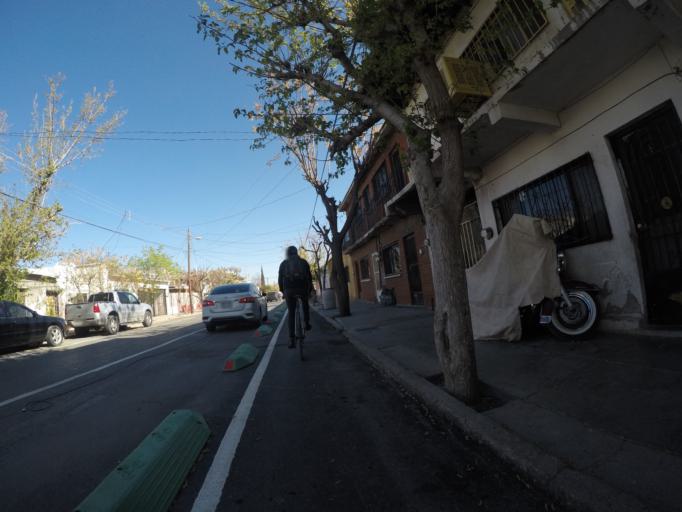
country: MX
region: Chihuahua
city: Ciudad Juarez
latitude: 31.7347
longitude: -106.4725
